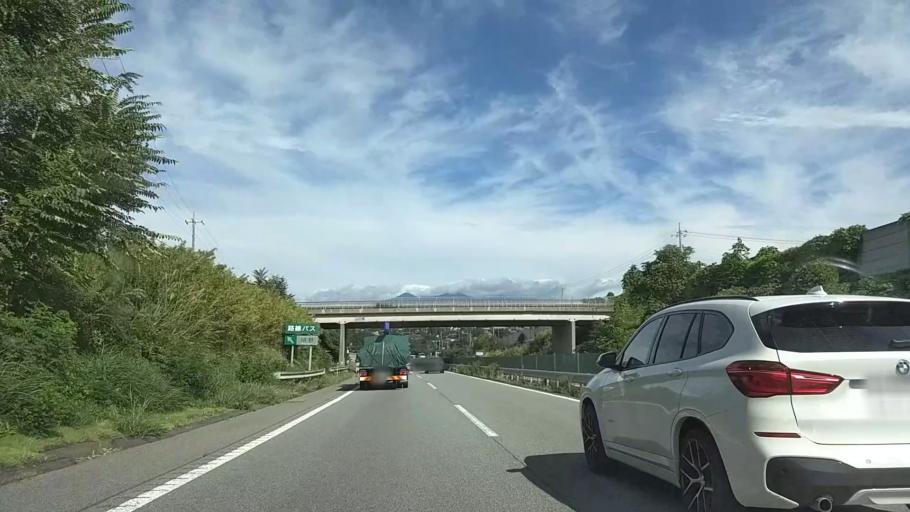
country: JP
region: Yamanashi
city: Nirasaki
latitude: 35.7516
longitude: 138.4416
